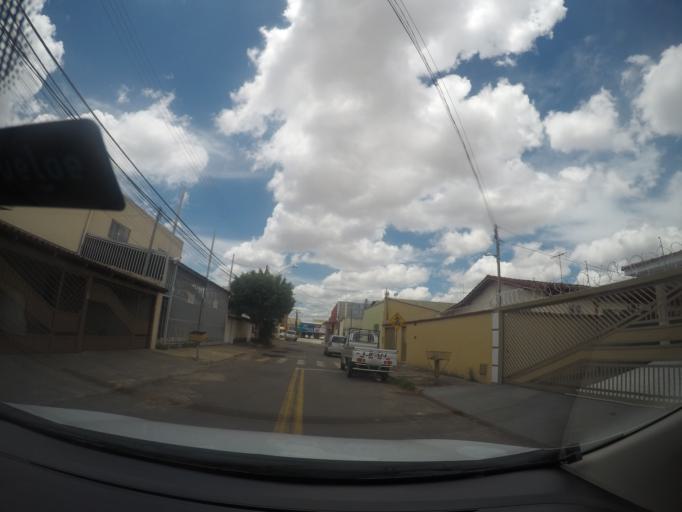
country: BR
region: Goias
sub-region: Goiania
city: Goiania
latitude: -16.6741
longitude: -49.3072
